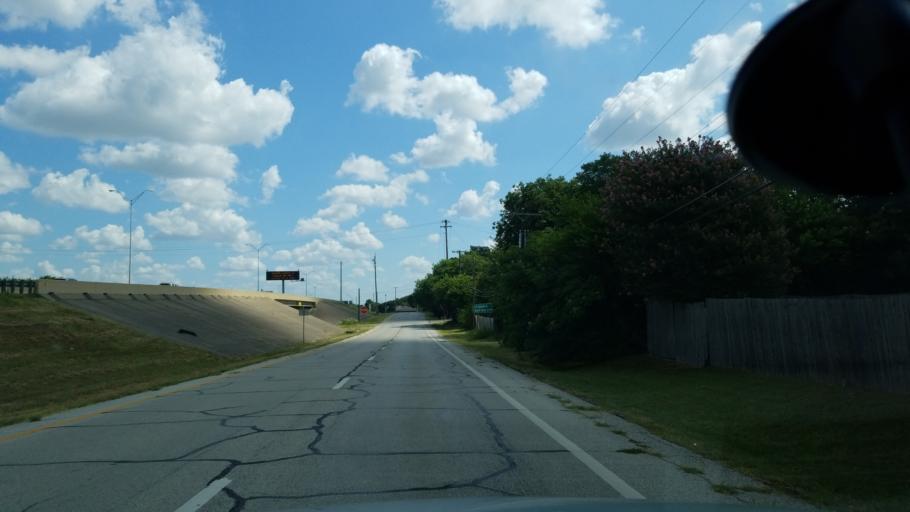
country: US
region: Texas
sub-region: Dallas County
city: Cockrell Hill
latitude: 32.6832
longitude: -96.8506
